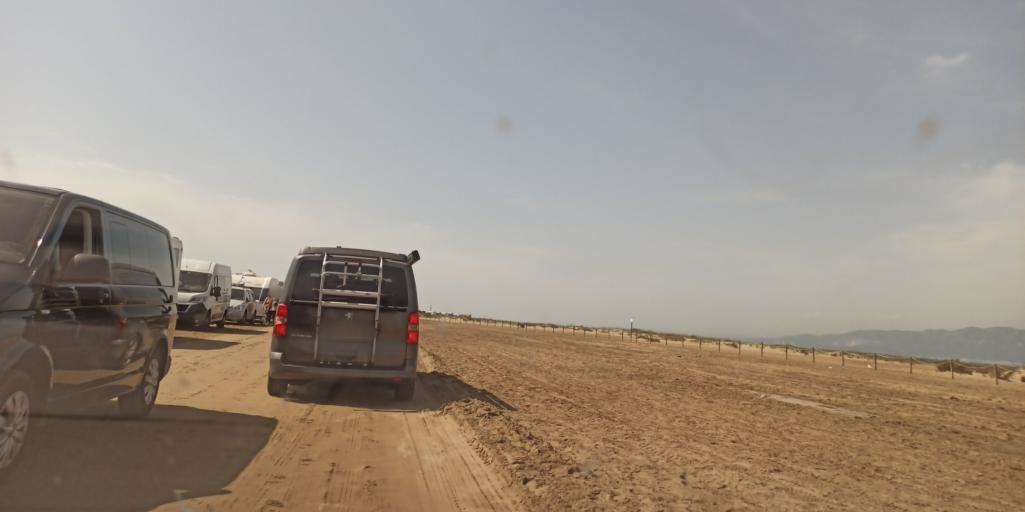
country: ES
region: Catalonia
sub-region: Provincia de Tarragona
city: Deltebre
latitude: 40.6328
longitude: 0.7459
